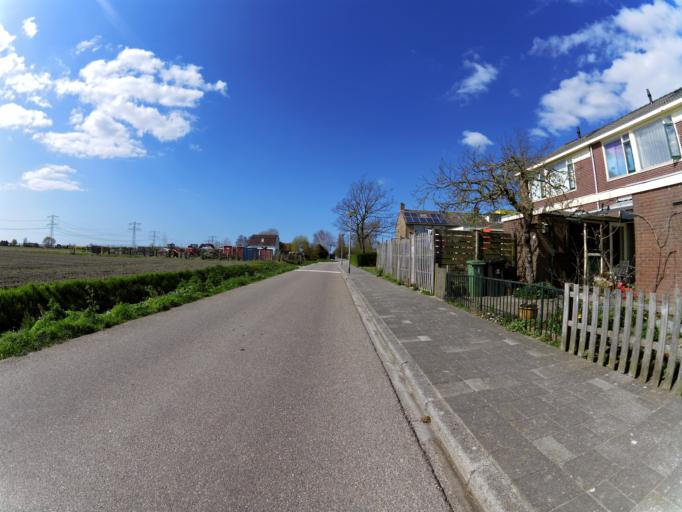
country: NL
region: South Holland
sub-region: Gemeente Brielle
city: Brielle
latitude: 51.8999
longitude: 4.1483
